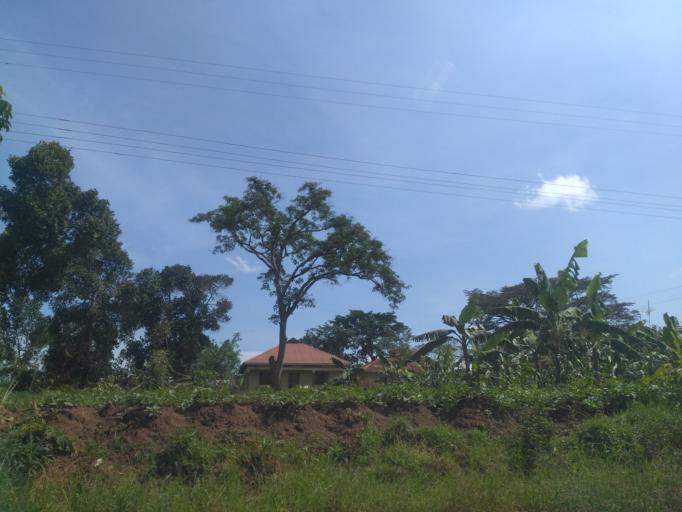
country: UG
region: Central Region
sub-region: Wakiso District
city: Kireka
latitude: 0.4498
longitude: 32.5831
